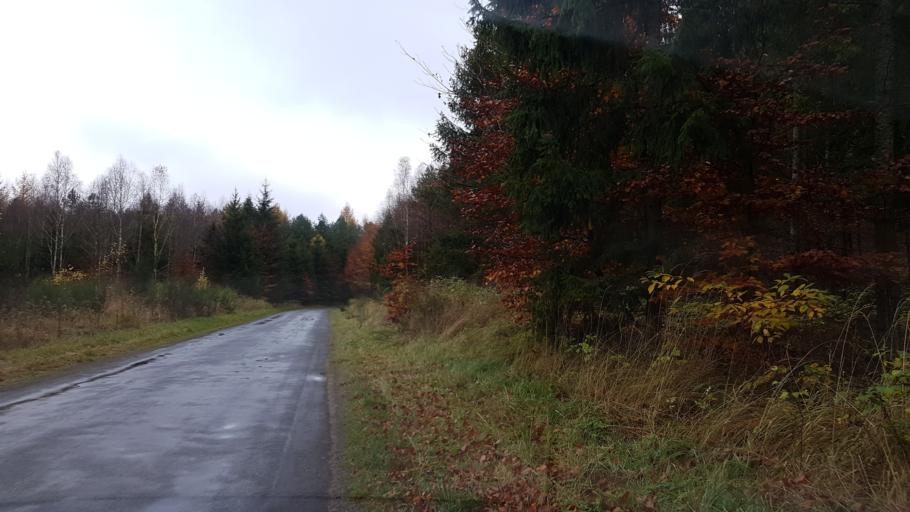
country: PL
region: West Pomeranian Voivodeship
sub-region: Powiat koszalinski
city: Polanow
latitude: 54.0771
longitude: 16.5766
